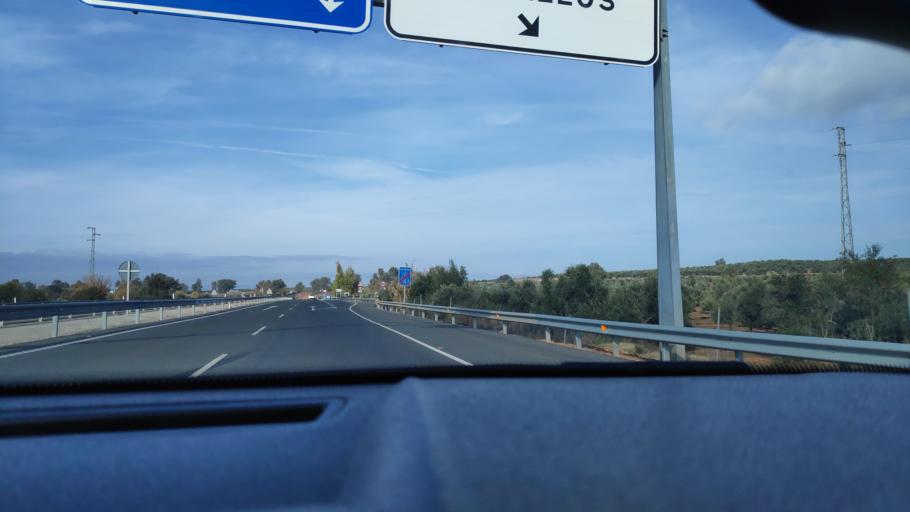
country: ES
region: Andalusia
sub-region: Provincia de Jaen
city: Linares
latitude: 38.0920
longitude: -3.6782
